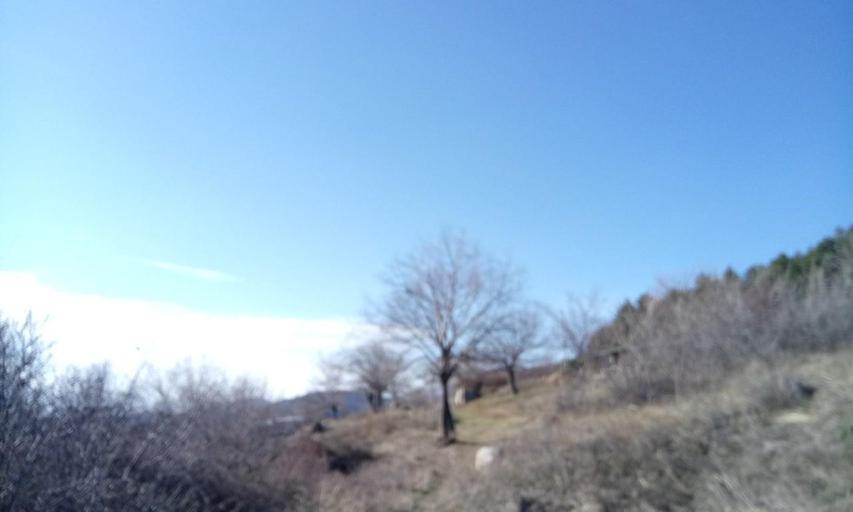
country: BG
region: Plovdiv
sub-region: Obshtina Khisarya
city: Khisarya
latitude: 42.5250
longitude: 24.7184
